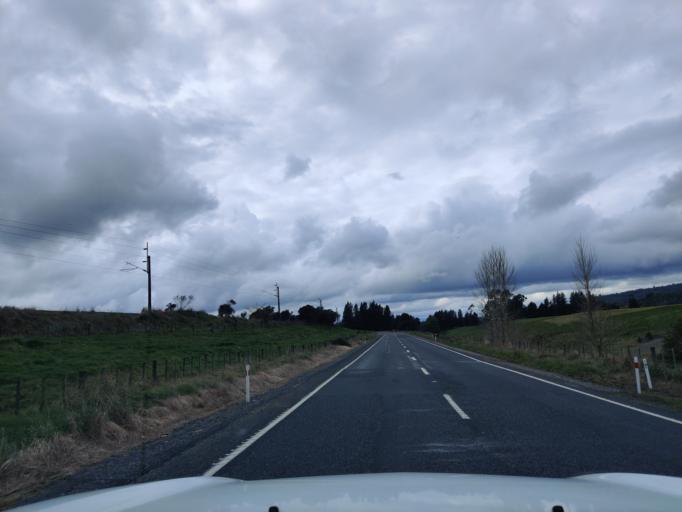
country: NZ
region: Waikato
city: Turangi
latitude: -39.0308
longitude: 175.3818
